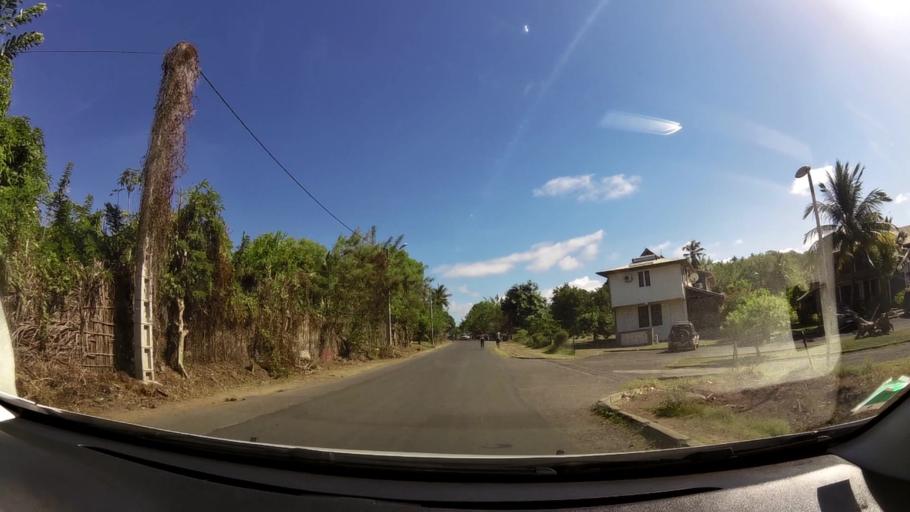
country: YT
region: Pamandzi
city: Pamandzi
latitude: -12.7812
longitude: 45.2792
